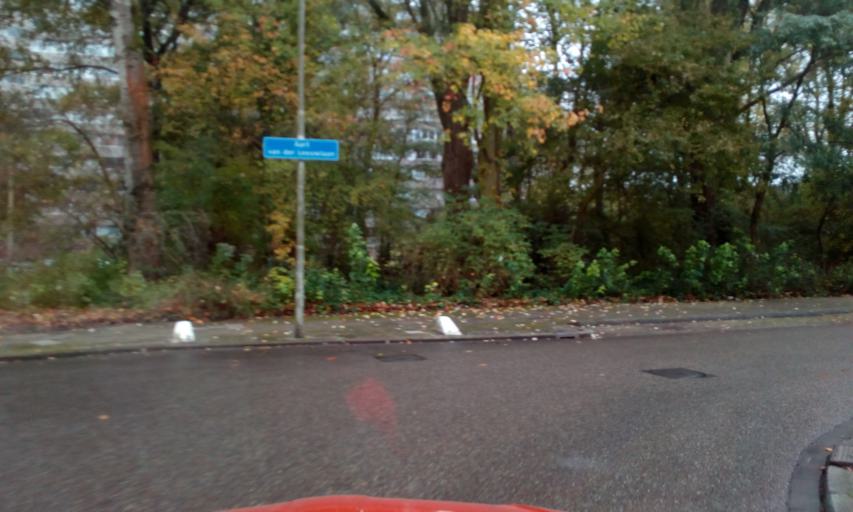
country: NL
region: South Holland
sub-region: Gemeente Delft
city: Delft
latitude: 51.9898
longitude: 4.3537
